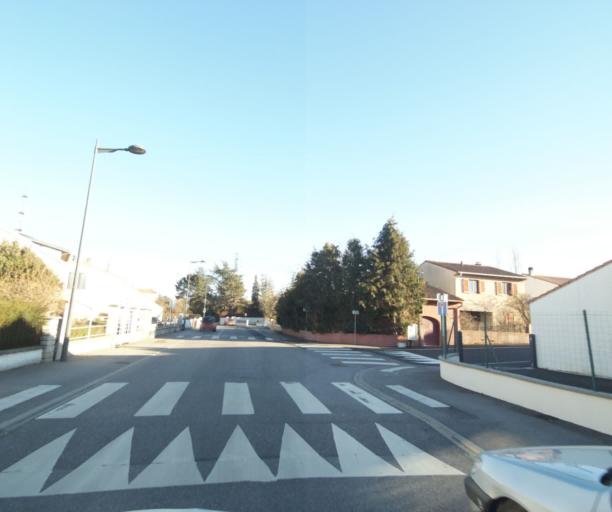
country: FR
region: Lorraine
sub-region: Departement de Meurthe-et-Moselle
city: Laneuveville-devant-Nancy
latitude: 48.6497
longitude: 6.2306
